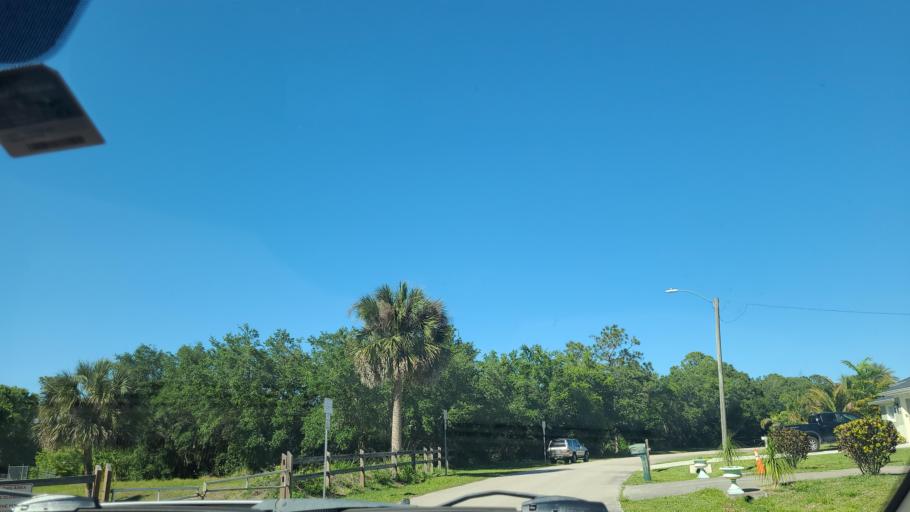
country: US
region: Florida
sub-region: Indian River County
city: Sebastian
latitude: 27.7655
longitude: -80.5017
